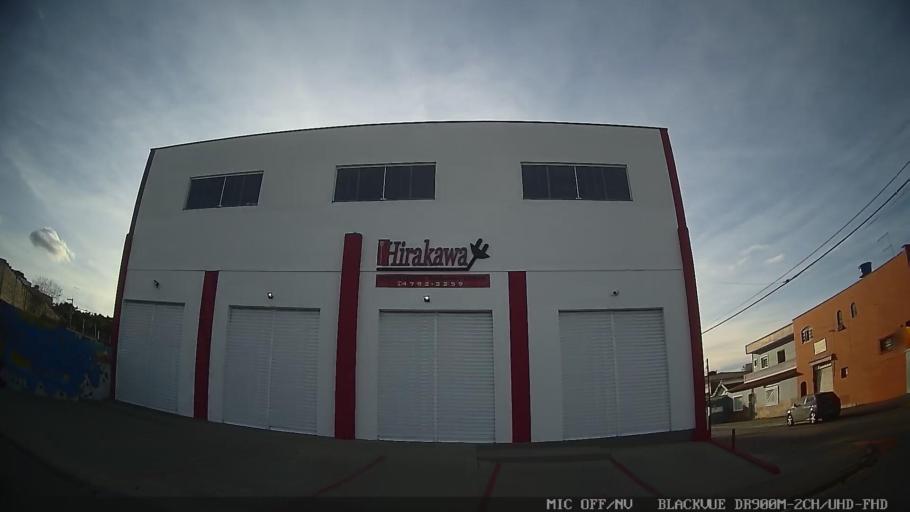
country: BR
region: Sao Paulo
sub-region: Mogi das Cruzes
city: Mogi das Cruzes
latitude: -23.5104
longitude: -46.1436
